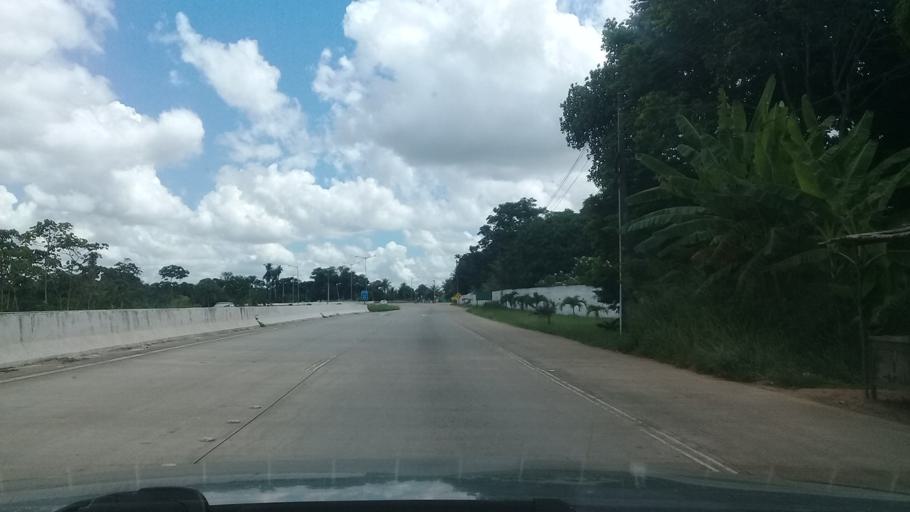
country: BR
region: Pernambuco
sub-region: Sao Lourenco Da Mata
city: Sao Lourenco da Mata
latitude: -7.9359
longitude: -35.1289
